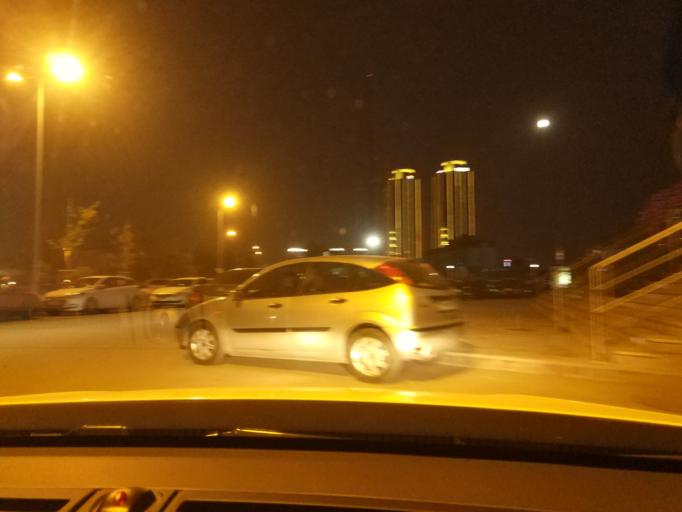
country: TR
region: Ankara
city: Batikent
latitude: 39.9100
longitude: 32.7553
